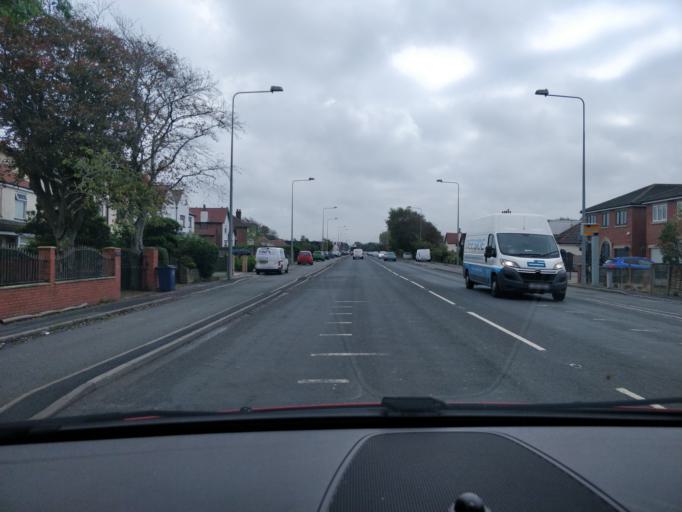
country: GB
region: England
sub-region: Sefton
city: Southport
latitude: 53.6304
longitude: -2.9672
